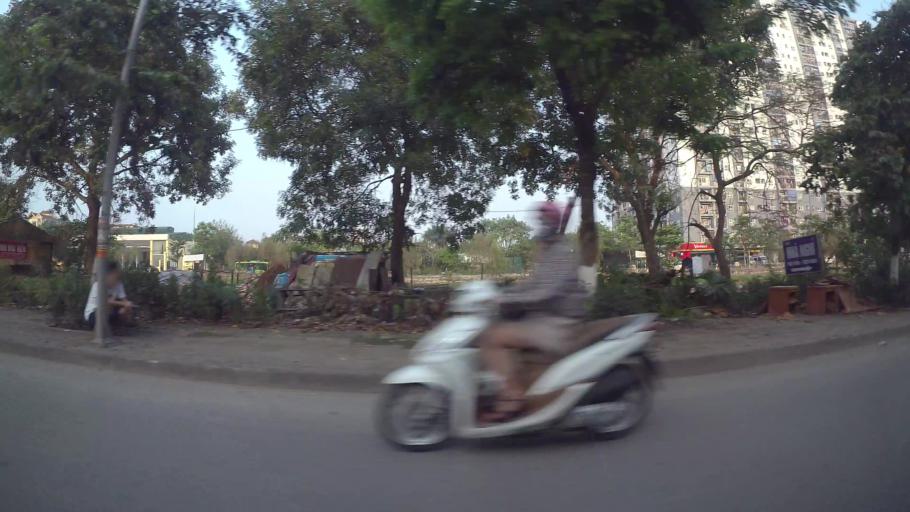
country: VN
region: Ha Noi
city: Thanh Xuan
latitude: 20.9755
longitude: 105.8248
